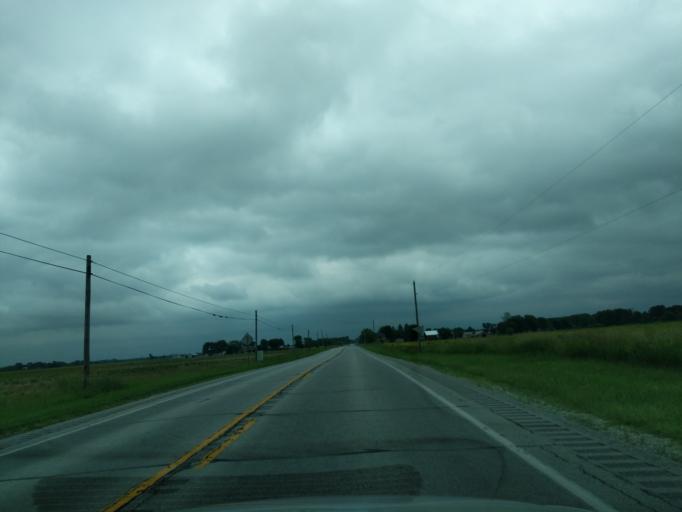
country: US
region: Indiana
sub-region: Madison County
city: Frankton
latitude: 40.2774
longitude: -85.7644
